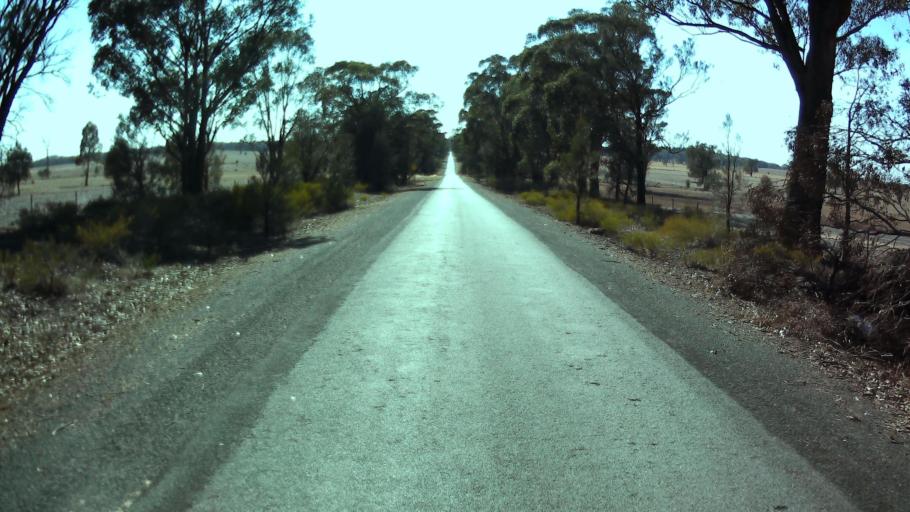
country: AU
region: New South Wales
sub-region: Weddin
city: Grenfell
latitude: -33.7824
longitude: 147.9659
